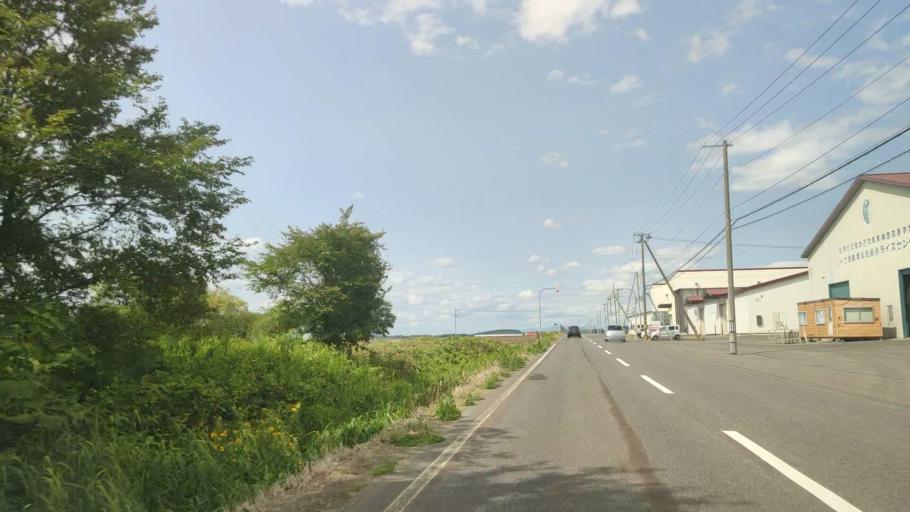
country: JP
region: Hokkaido
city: Nayoro
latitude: 44.2039
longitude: 142.4158
